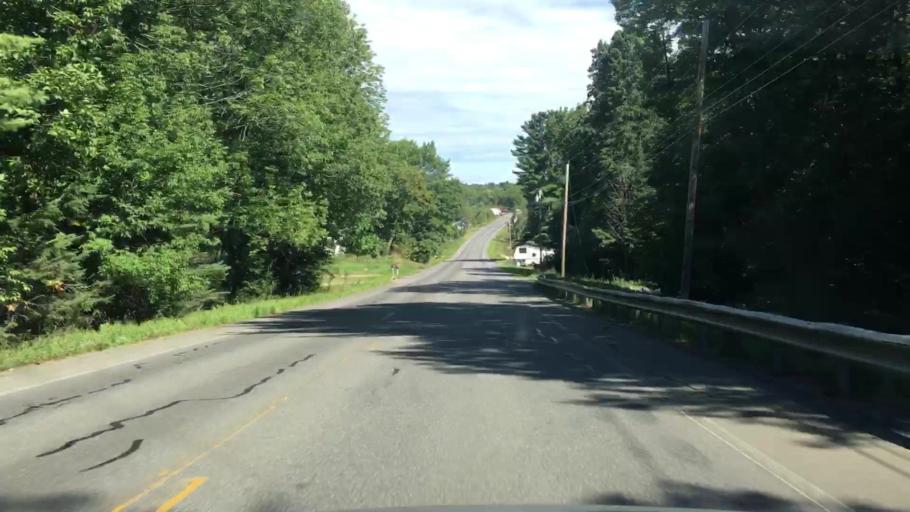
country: US
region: Maine
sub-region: Penobscot County
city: Dexter
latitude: 45.0777
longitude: -69.2310
